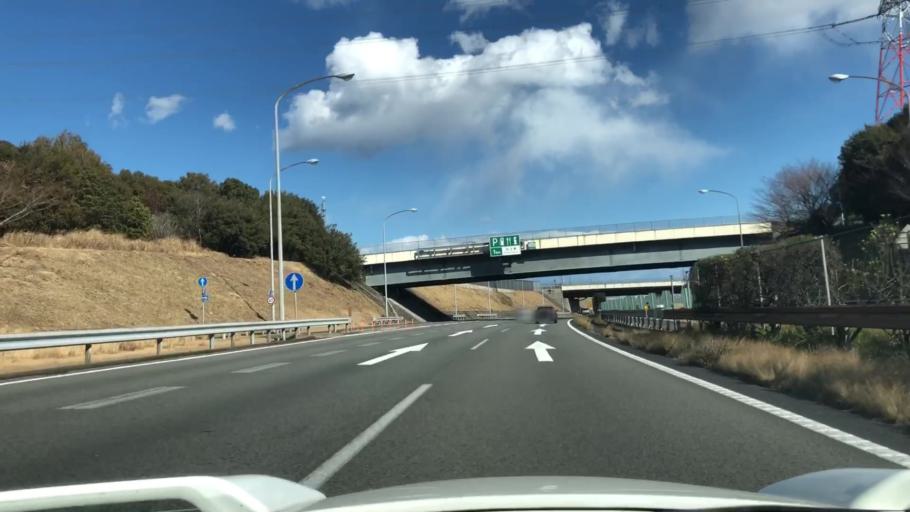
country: JP
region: Shizuoka
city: Kanaya
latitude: 34.7617
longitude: 138.1381
